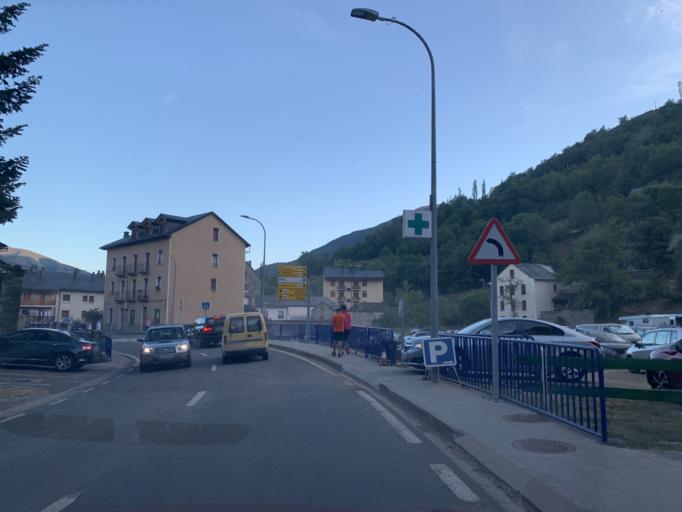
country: ES
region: Aragon
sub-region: Provincia de Huesca
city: Broto
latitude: 42.6056
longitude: -0.1238
